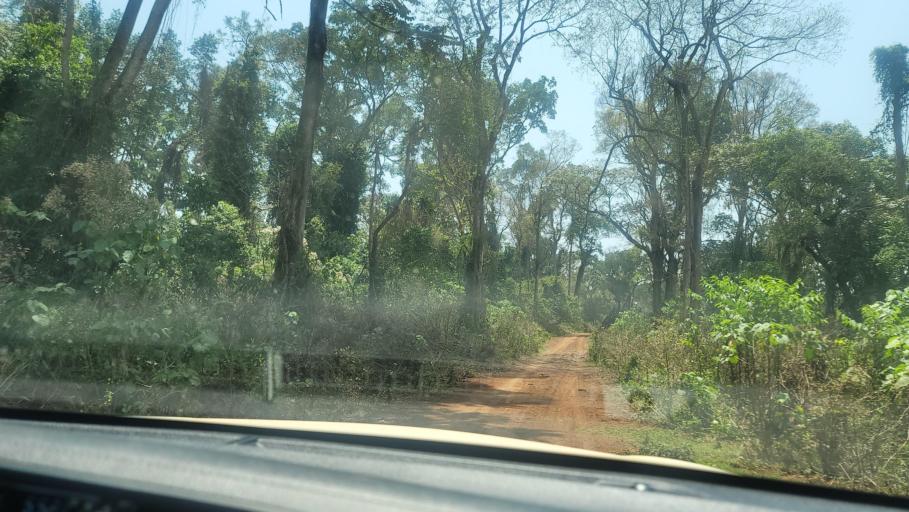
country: ET
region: Southern Nations, Nationalities, and People's Region
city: Bonga
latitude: 7.5440
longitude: 36.1788
